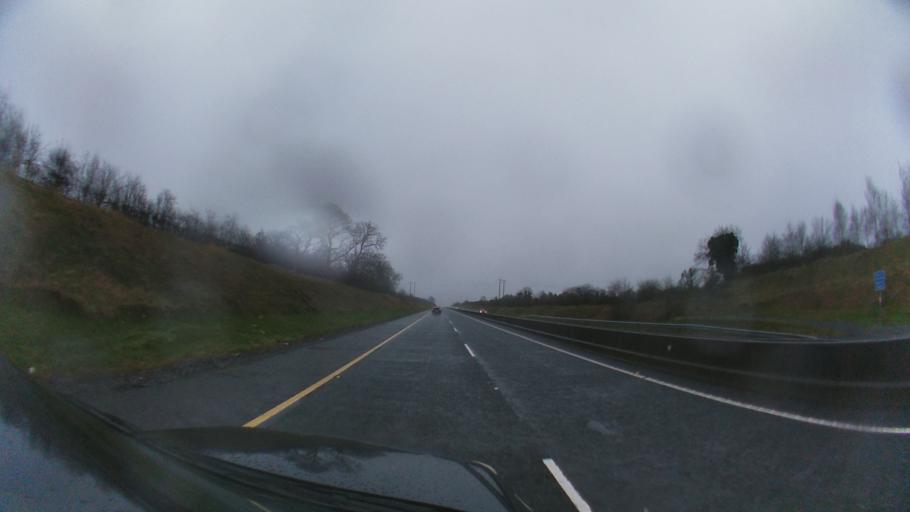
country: IE
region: Leinster
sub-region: Kildare
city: Castledermot
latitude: 52.8390
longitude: -6.8448
